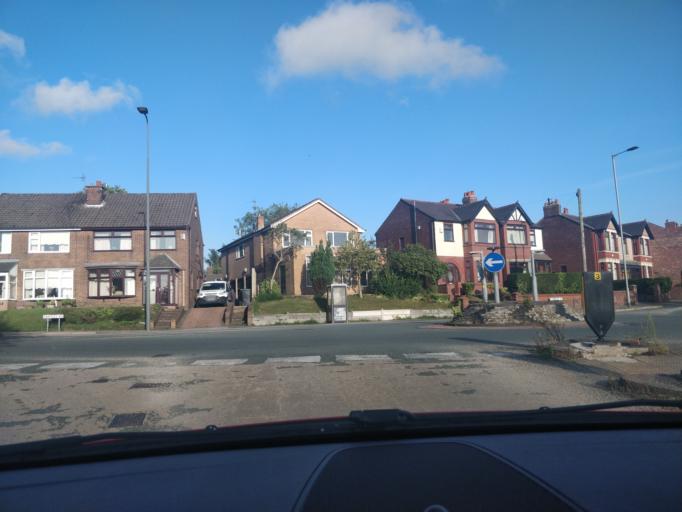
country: GB
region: England
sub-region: St. Helens
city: Billinge
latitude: 53.5261
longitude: -2.7163
